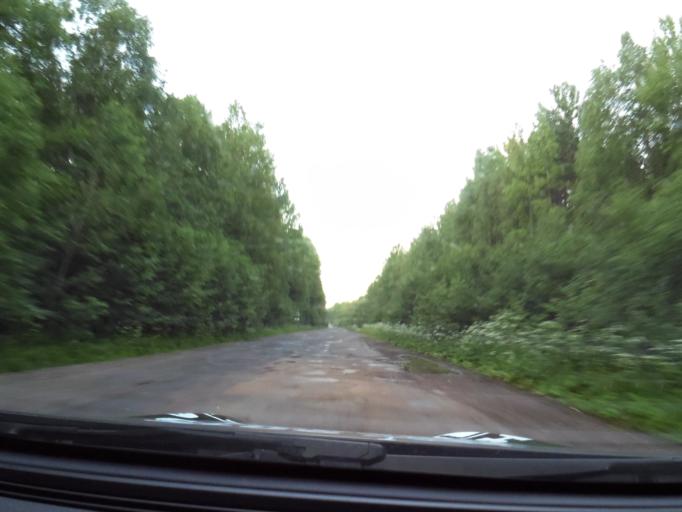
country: RU
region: Leningrad
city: Voznesen'ye
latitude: 60.8392
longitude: 35.6422
